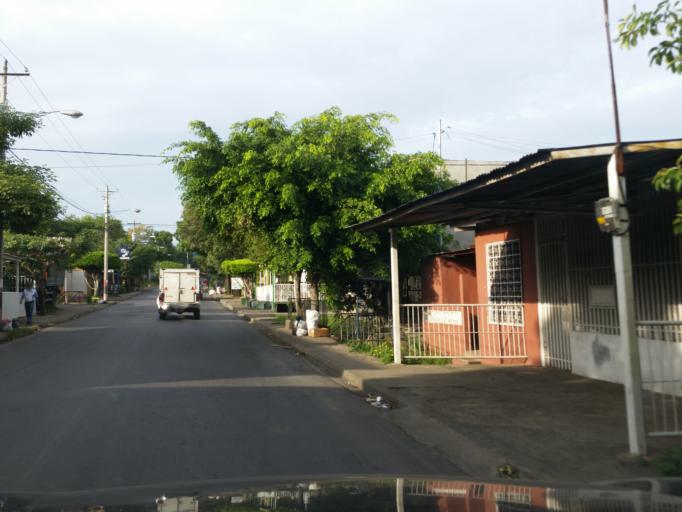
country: NI
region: Managua
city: Managua
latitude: 12.1264
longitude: -86.2083
